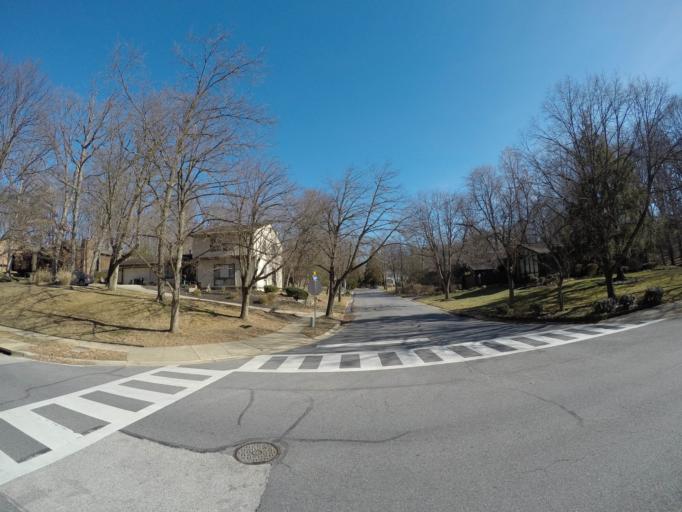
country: US
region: Maryland
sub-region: Howard County
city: Columbia
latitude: 39.2213
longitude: -76.8125
